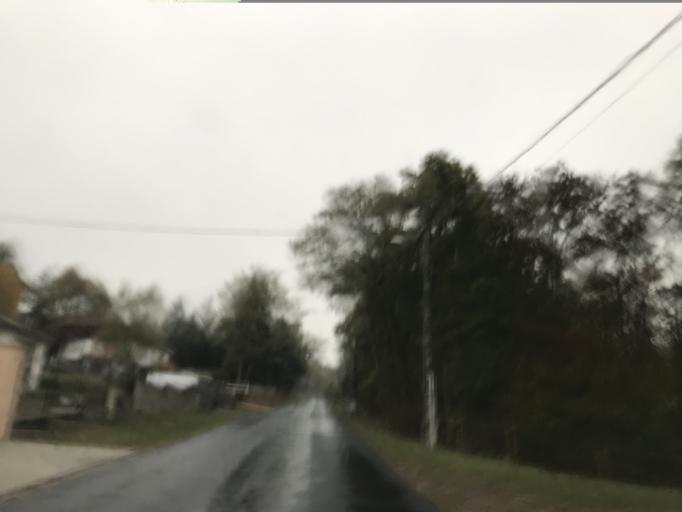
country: FR
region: Auvergne
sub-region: Departement du Puy-de-Dome
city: Courpiere
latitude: 45.7523
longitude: 3.5561
